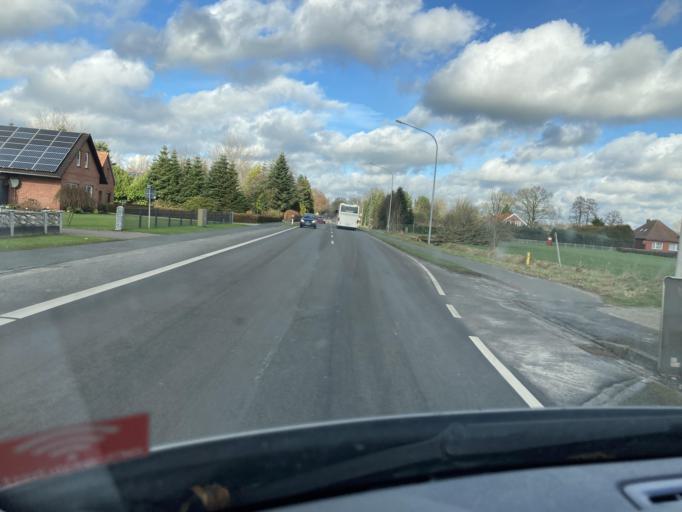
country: DE
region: Lower Saxony
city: Ostrhauderfehn
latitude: 53.1463
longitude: 7.5644
